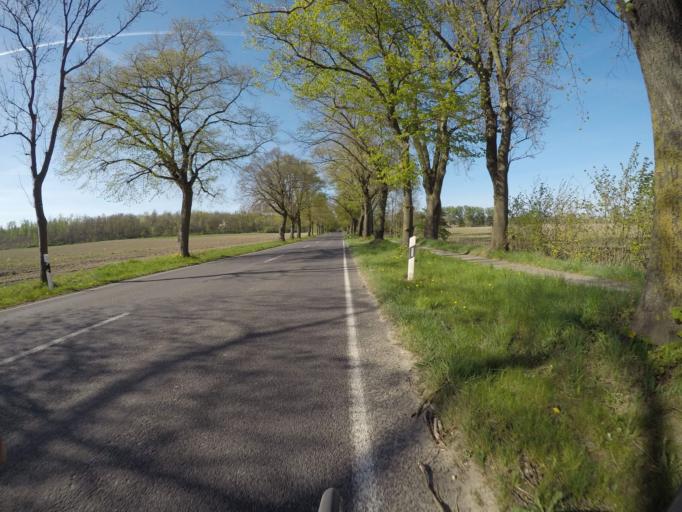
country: DE
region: Brandenburg
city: Grunheide
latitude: 52.4683
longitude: 13.8567
